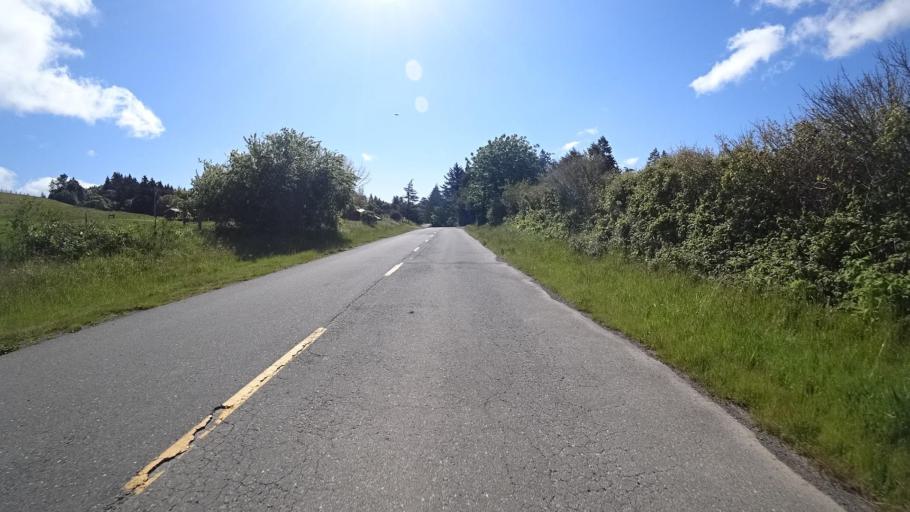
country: US
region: California
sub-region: Humboldt County
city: Ferndale
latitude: 40.3428
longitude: -124.3213
